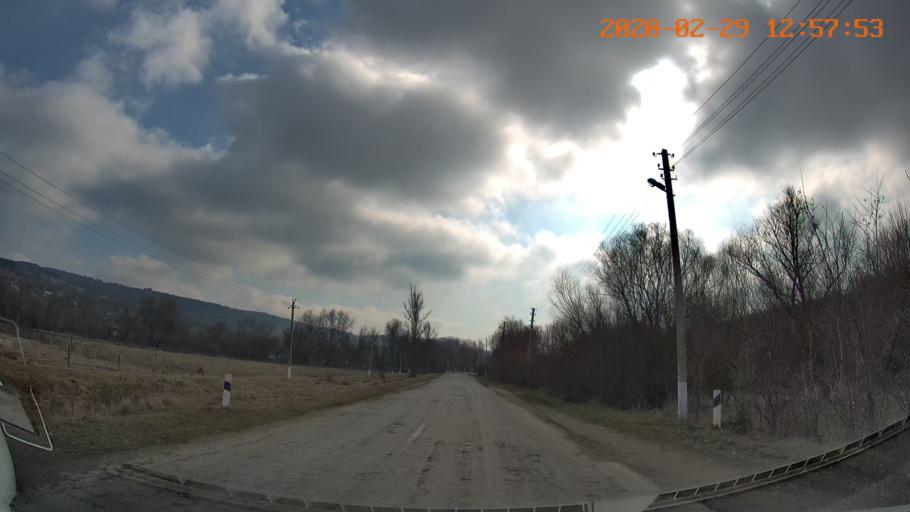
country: MD
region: Telenesti
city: Camenca
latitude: 48.0735
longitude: 28.7172
